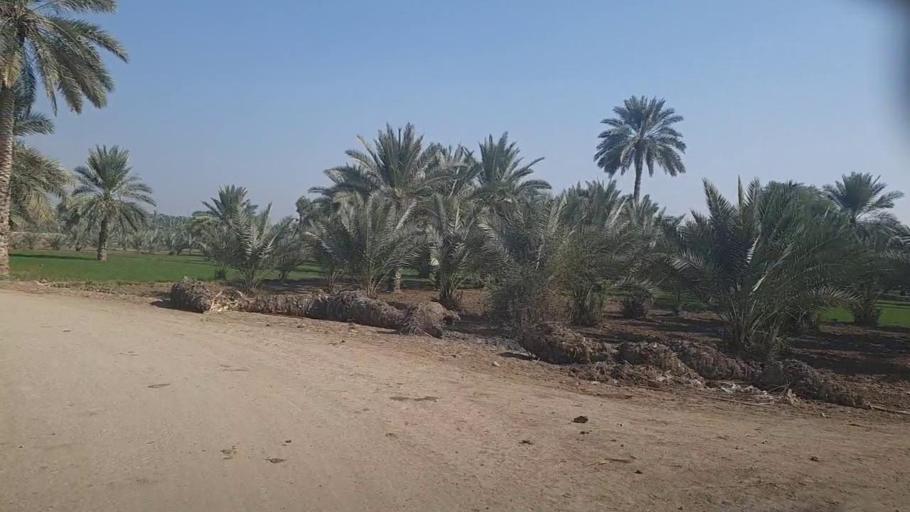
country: PK
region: Sindh
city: Kot Diji
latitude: 27.4237
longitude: 68.7072
